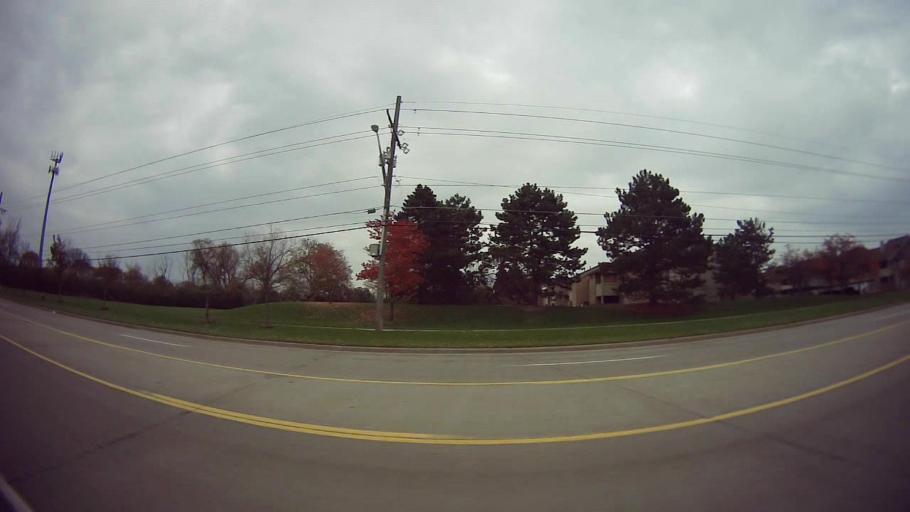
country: US
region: Michigan
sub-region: Macomb County
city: Sterling Heights
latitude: 42.5486
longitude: -83.0693
